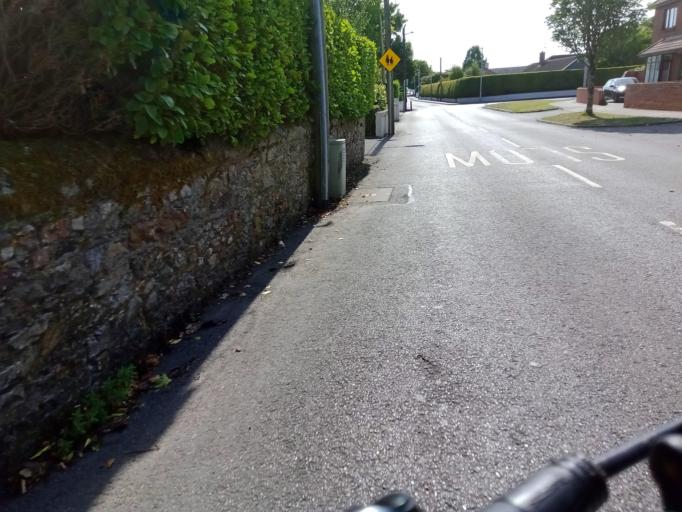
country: IE
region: Munster
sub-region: Waterford
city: Dungarvan
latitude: 52.0905
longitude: -7.6089
